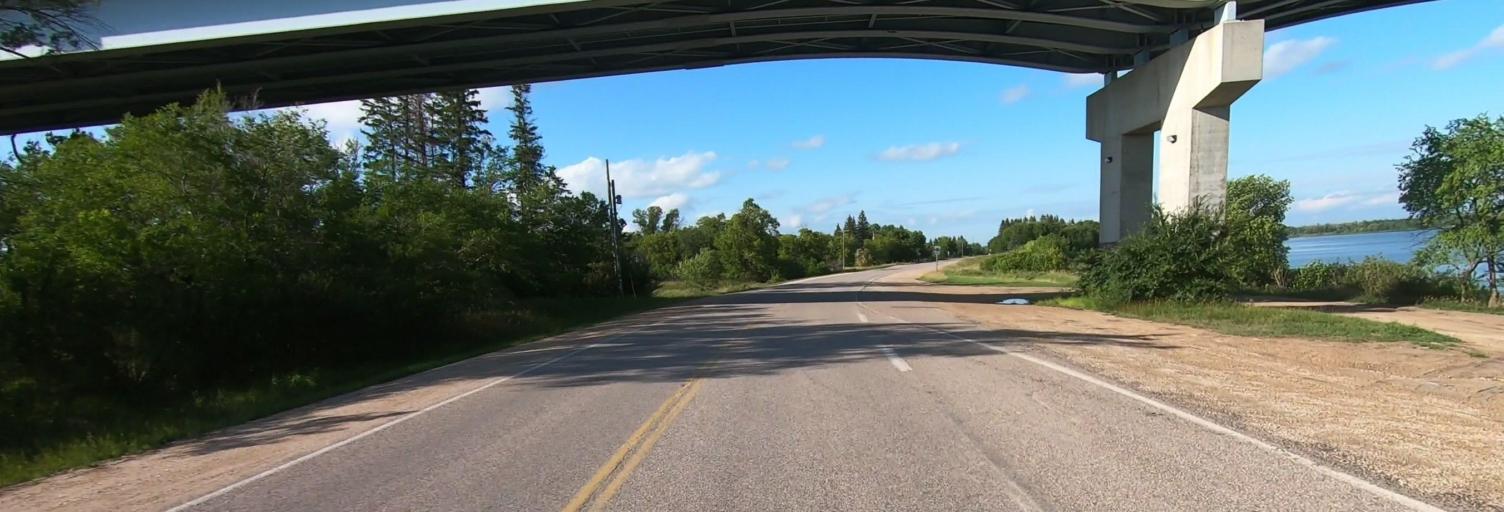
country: CA
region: Manitoba
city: Selkirk
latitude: 50.1908
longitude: -96.8452
